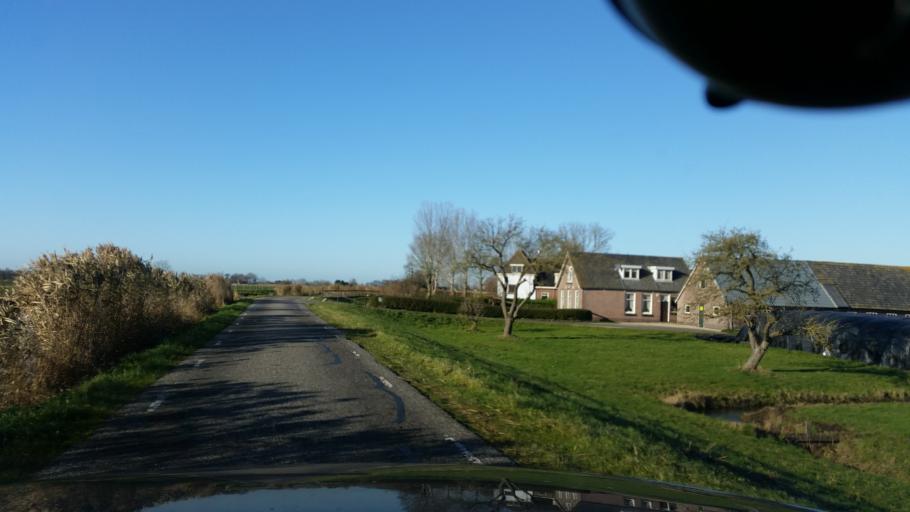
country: NL
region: North Holland
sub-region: Gemeente Ouder-Amstel
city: Ouderkerk aan de Amstel
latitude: 52.2512
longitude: 4.8979
